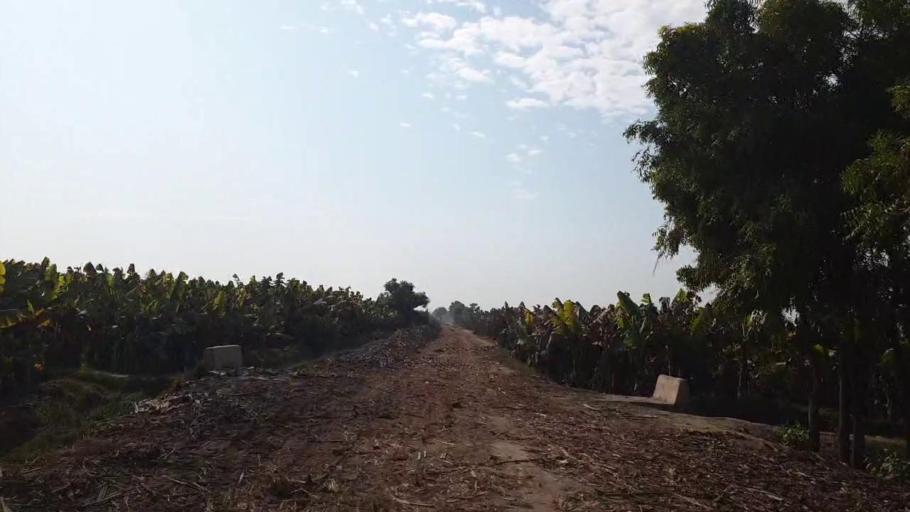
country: PK
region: Sindh
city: Matiari
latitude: 25.5503
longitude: 68.5159
